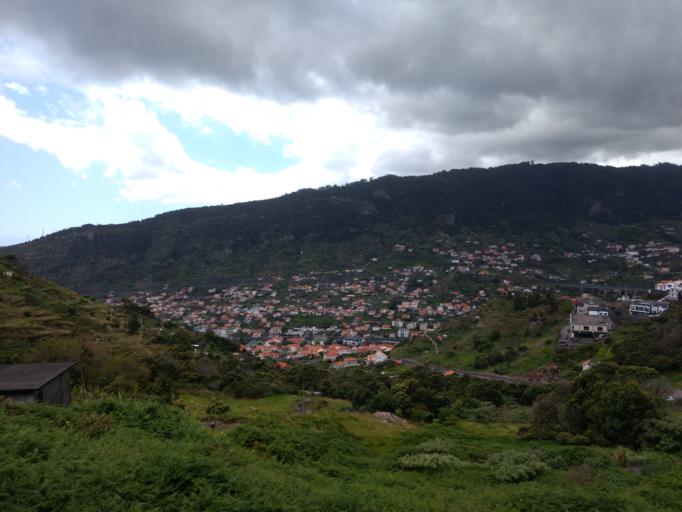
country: PT
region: Madeira
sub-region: Machico
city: Canical
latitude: 32.7325
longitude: -16.7639
